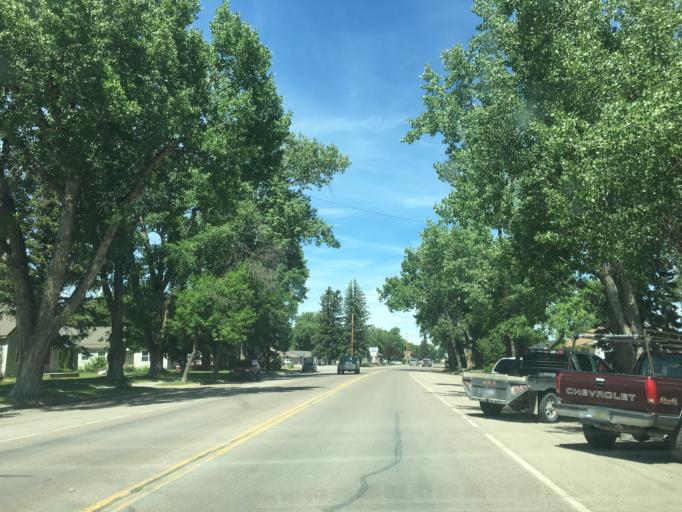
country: US
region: Montana
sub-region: Teton County
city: Choteau
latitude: 47.8161
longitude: -112.1867
